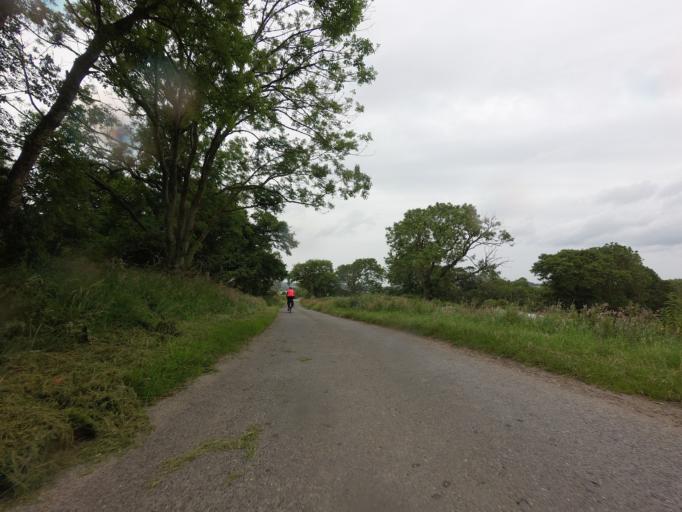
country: GB
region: Scotland
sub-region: Moray
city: Cullen
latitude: 57.6707
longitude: -2.7713
